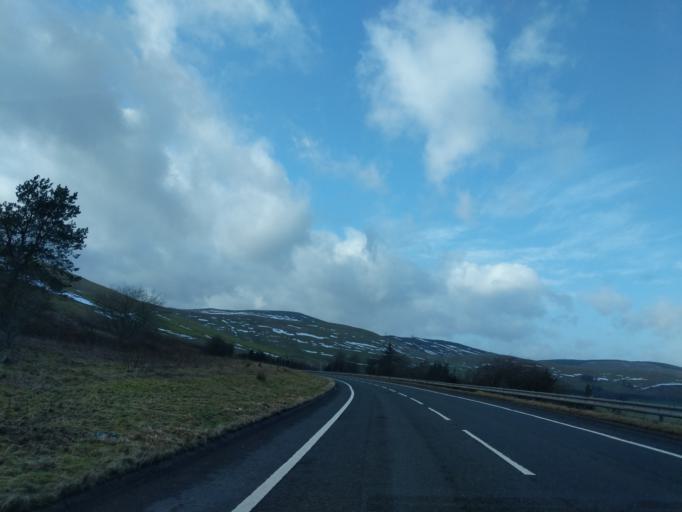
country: GB
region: Scotland
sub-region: South Lanarkshire
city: Douglas
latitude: 55.4684
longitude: -3.6608
